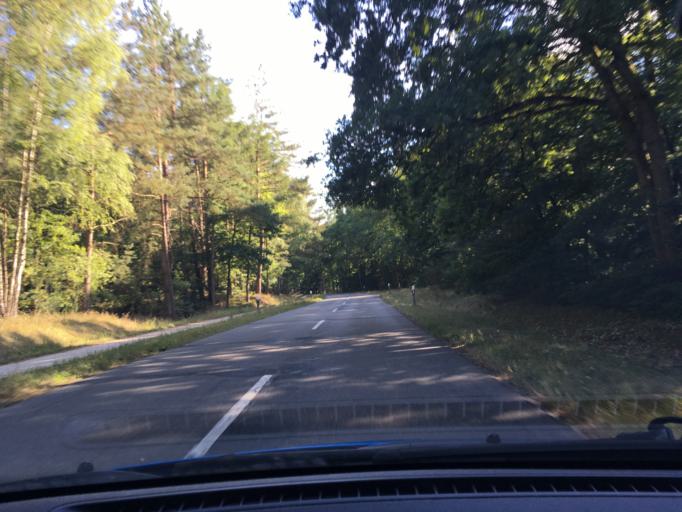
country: DE
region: Lower Saxony
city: Bleckede
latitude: 53.2762
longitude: 10.7201
